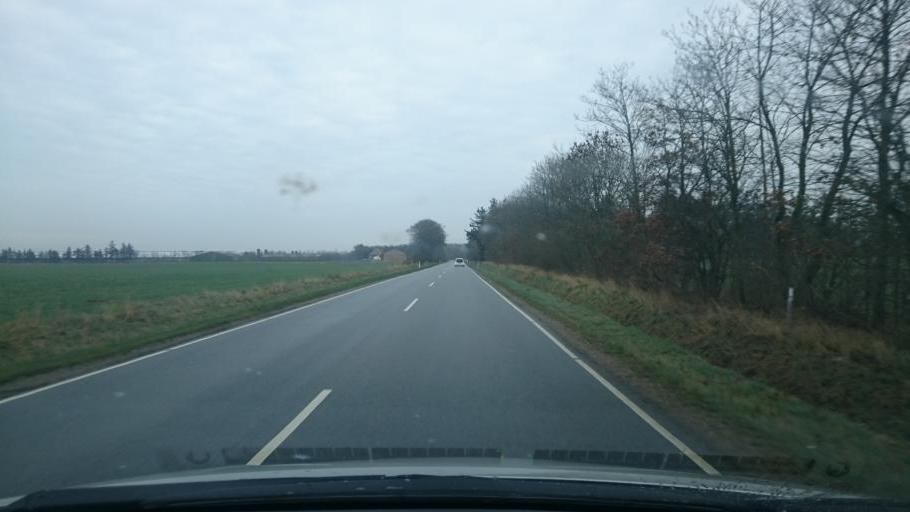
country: DK
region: South Denmark
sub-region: Esbjerg Kommune
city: Ribe
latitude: 55.3344
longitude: 8.8211
